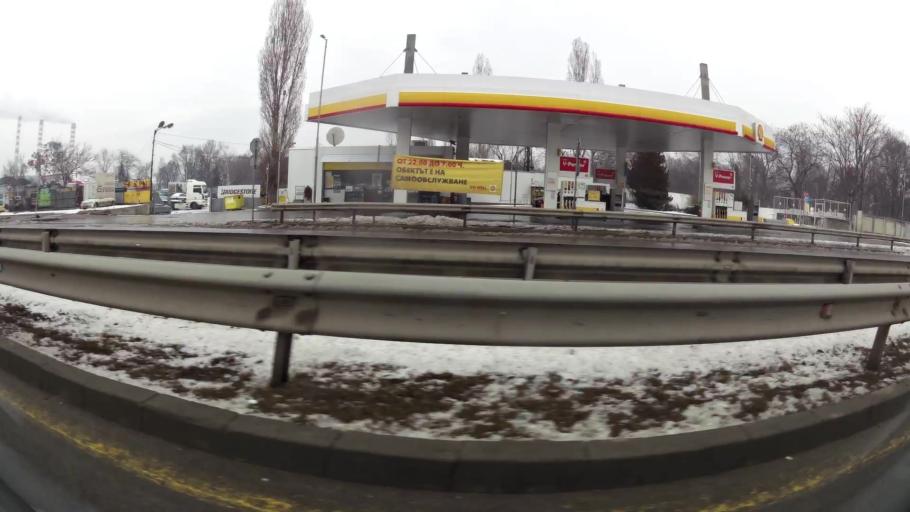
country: BG
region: Sofia-Capital
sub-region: Stolichna Obshtina
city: Sofia
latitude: 42.7141
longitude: 23.3277
